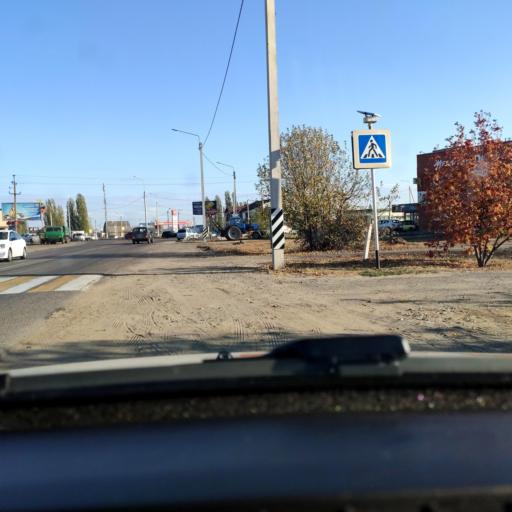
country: RU
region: Voronezj
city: Semiluki
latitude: 51.7262
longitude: 39.0337
